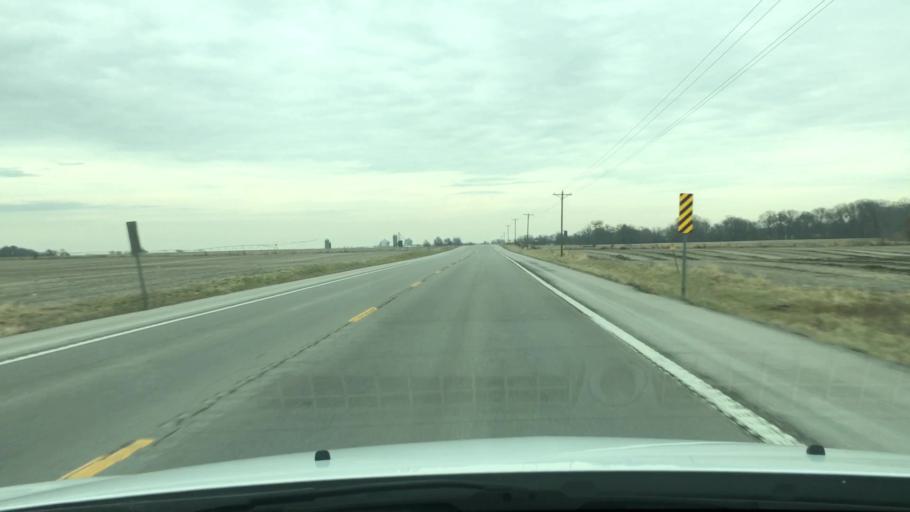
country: US
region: Missouri
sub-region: Audrain County
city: Mexico
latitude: 39.1643
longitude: -91.7167
